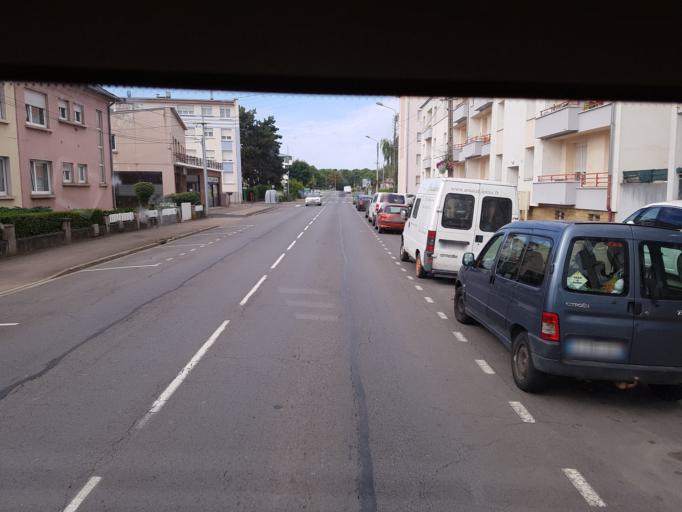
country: FR
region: Lorraine
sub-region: Departement de la Moselle
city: Yutz
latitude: 49.3550
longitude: 6.1823
